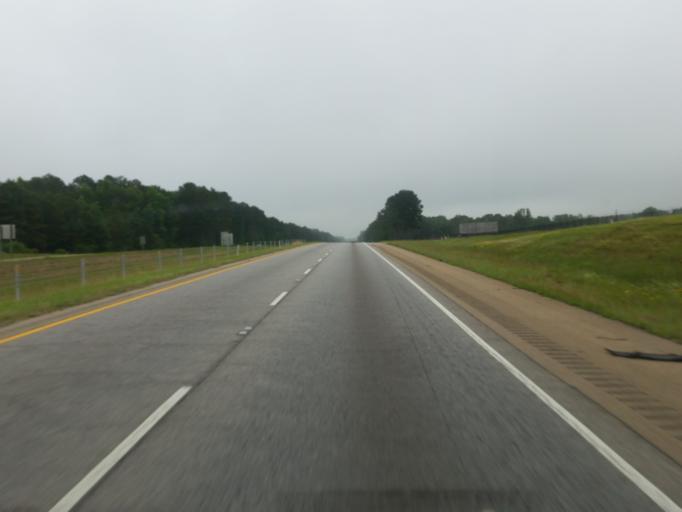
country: US
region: Louisiana
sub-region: Webster Parish
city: Minden
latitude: 32.5800
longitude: -93.2462
